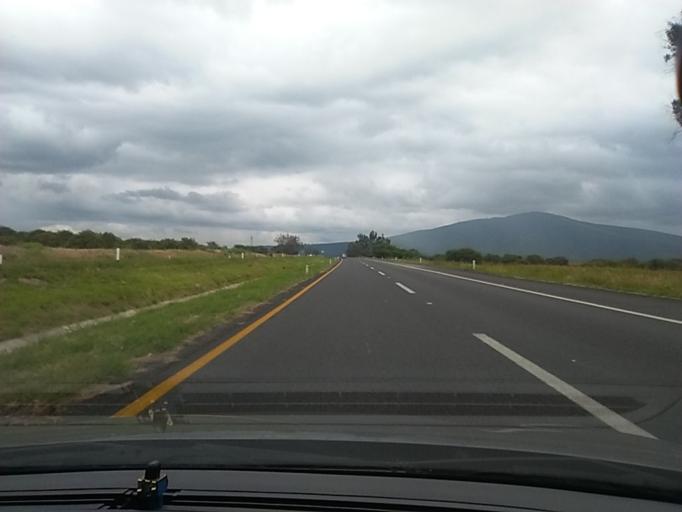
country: MX
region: Jalisco
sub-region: Zapotlanejo
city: La Mezquitera
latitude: 20.5706
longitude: -103.0830
